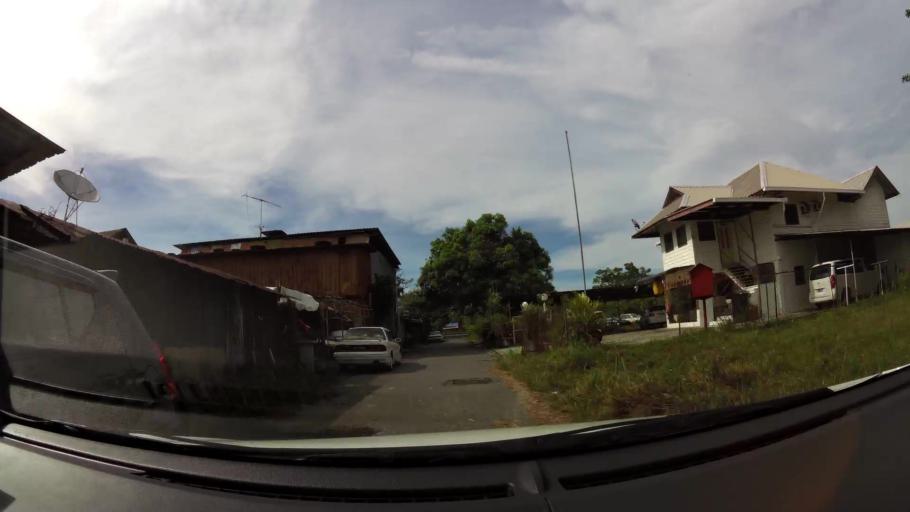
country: BN
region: Belait
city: Seria
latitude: 4.6141
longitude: 114.3338
